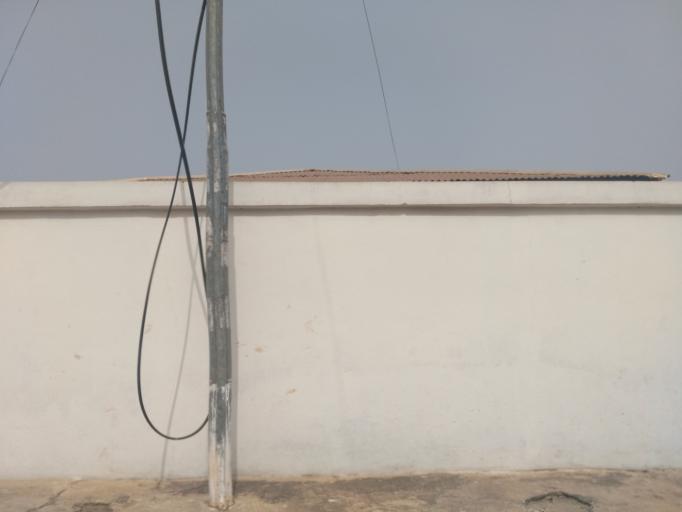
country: GH
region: Ashanti
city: Kumasi
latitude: 6.6753
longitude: -1.6012
